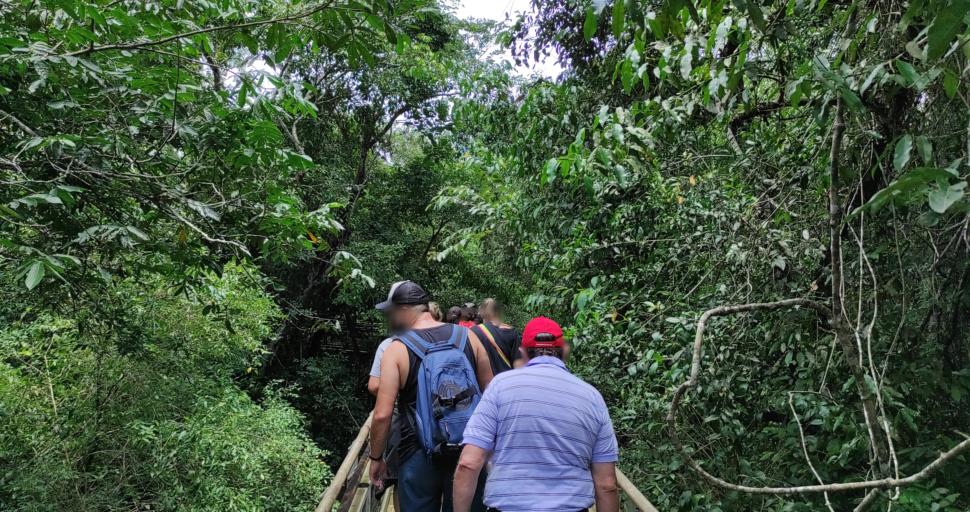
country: AR
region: Misiones
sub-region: Departamento de Iguazu
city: Puerto Iguazu
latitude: -25.6879
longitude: -54.4458
